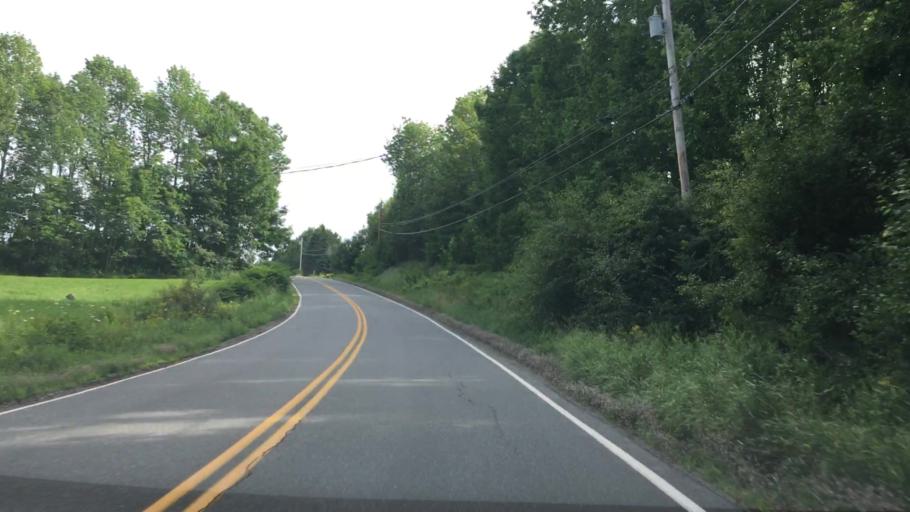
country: US
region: Maine
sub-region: Waldo County
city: Belfast
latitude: 44.3819
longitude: -69.0350
